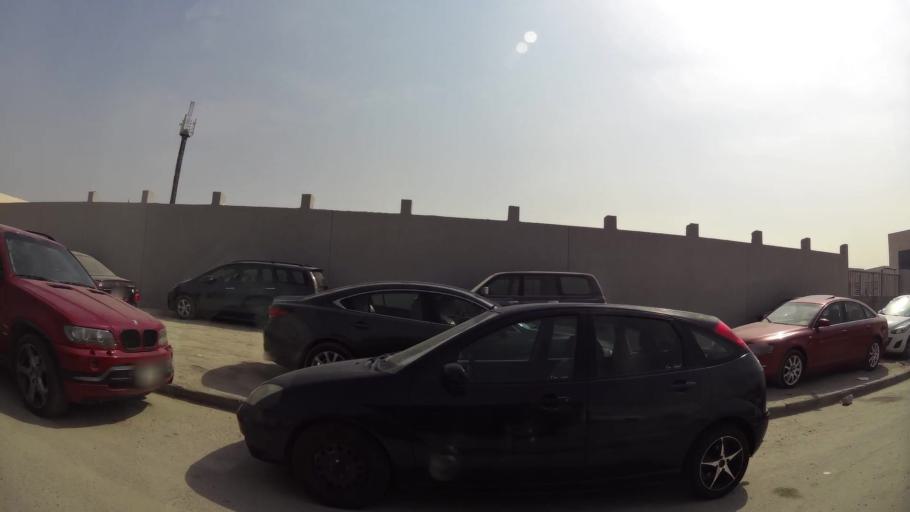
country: KW
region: Al Asimah
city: Ash Shamiyah
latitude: 29.3312
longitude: 47.9392
